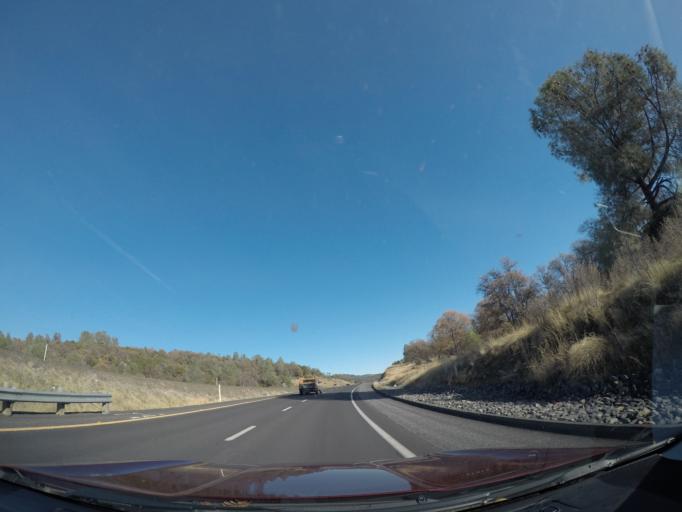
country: US
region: California
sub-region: Tuolumne County
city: East Sonora
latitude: 37.9770
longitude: -120.3554
